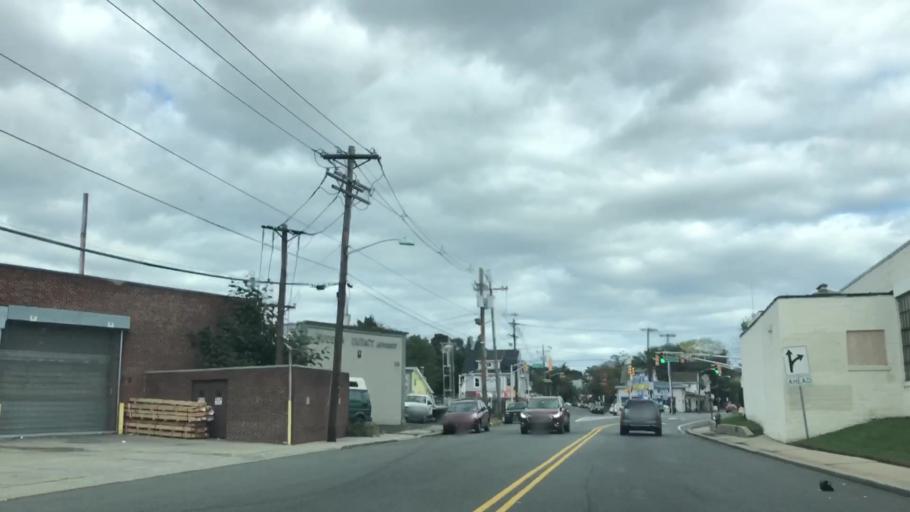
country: US
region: New Jersey
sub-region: Union County
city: Hillside
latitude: 40.7089
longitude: -74.2327
